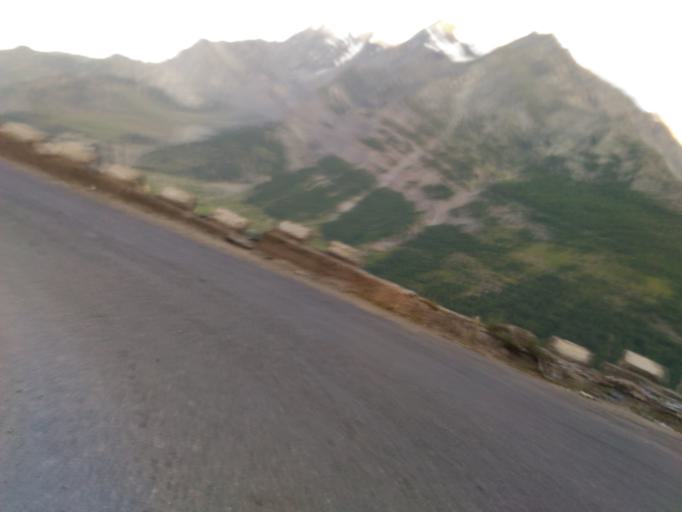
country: IN
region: Himachal Pradesh
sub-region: Lahul and Spiti
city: Kyelang
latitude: 32.5111
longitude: 77.0048
